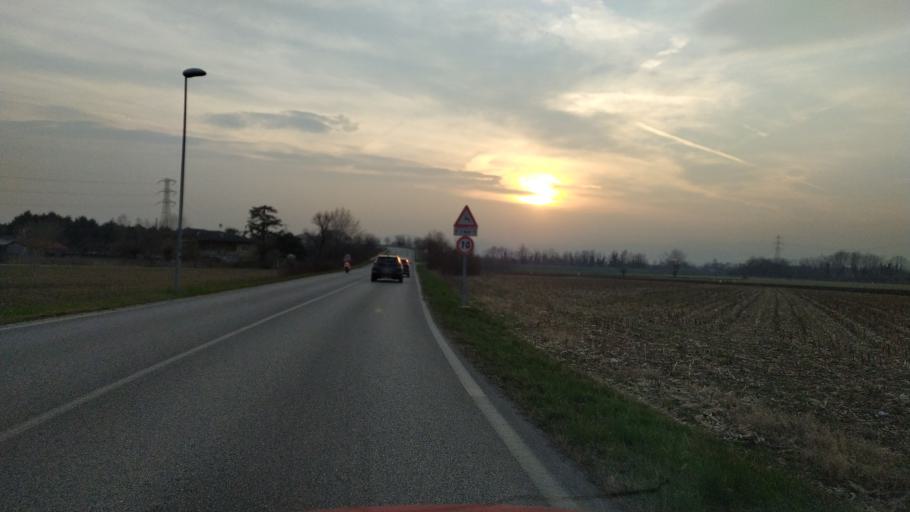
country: IT
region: Veneto
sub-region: Provincia di Vicenza
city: Montecchio Precalcino
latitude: 45.6525
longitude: 11.5570
